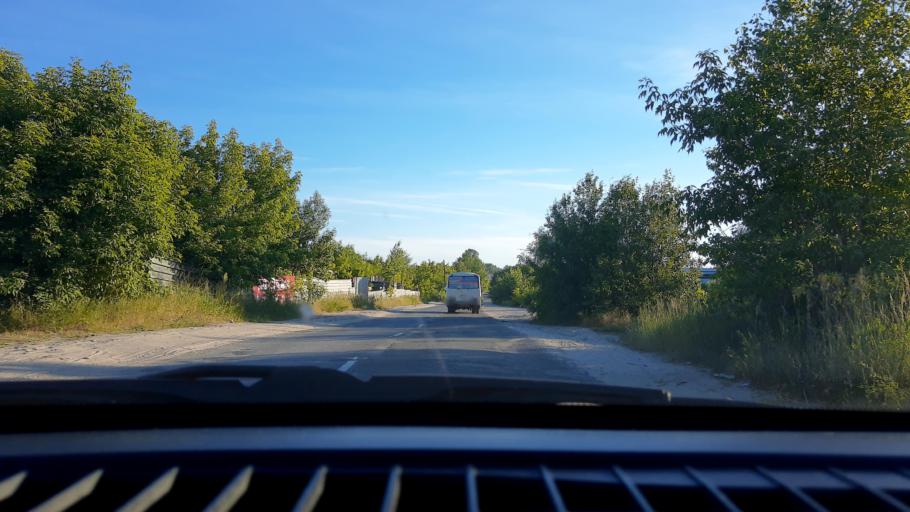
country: RU
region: Nizjnij Novgorod
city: Dzerzhinsk
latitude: 56.2474
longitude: 43.4992
